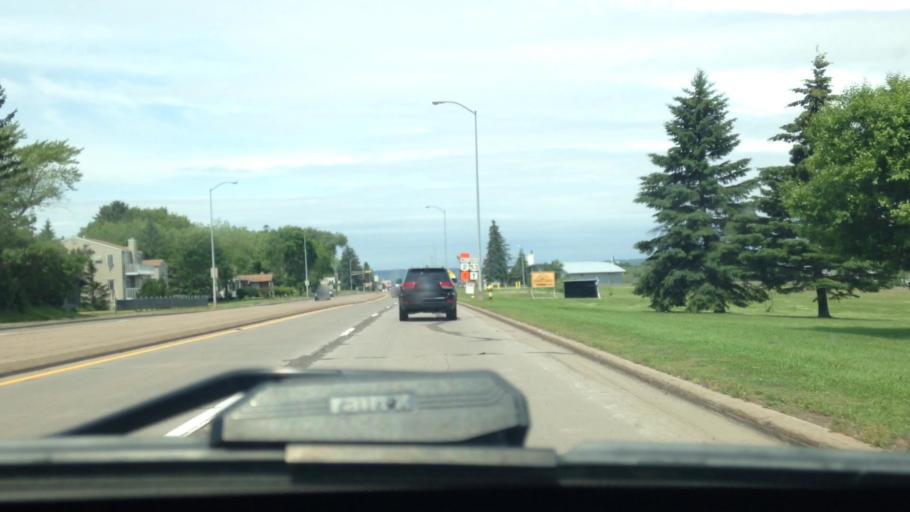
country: US
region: Wisconsin
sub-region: Douglas County
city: Superior
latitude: 46.7205
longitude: -92.0656
